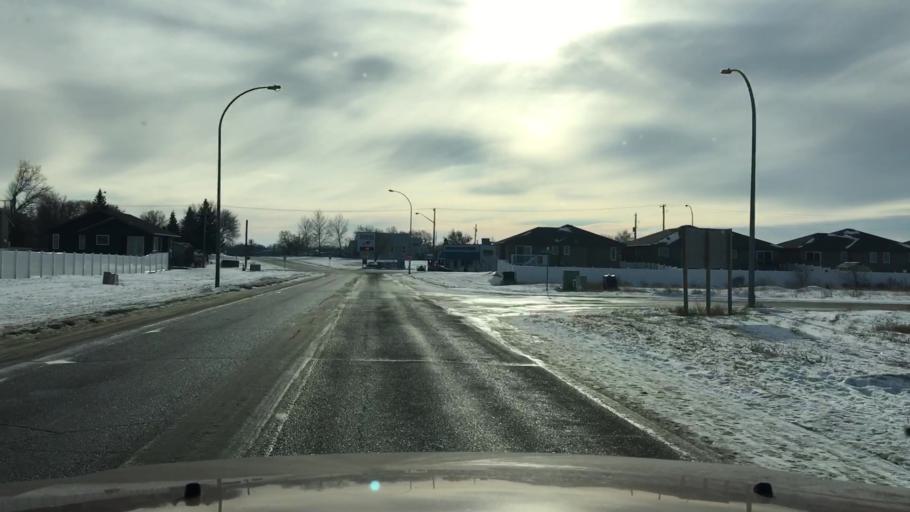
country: CA
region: Saskatchewan
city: Pilot Butte
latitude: 50.4855
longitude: -104.4202
